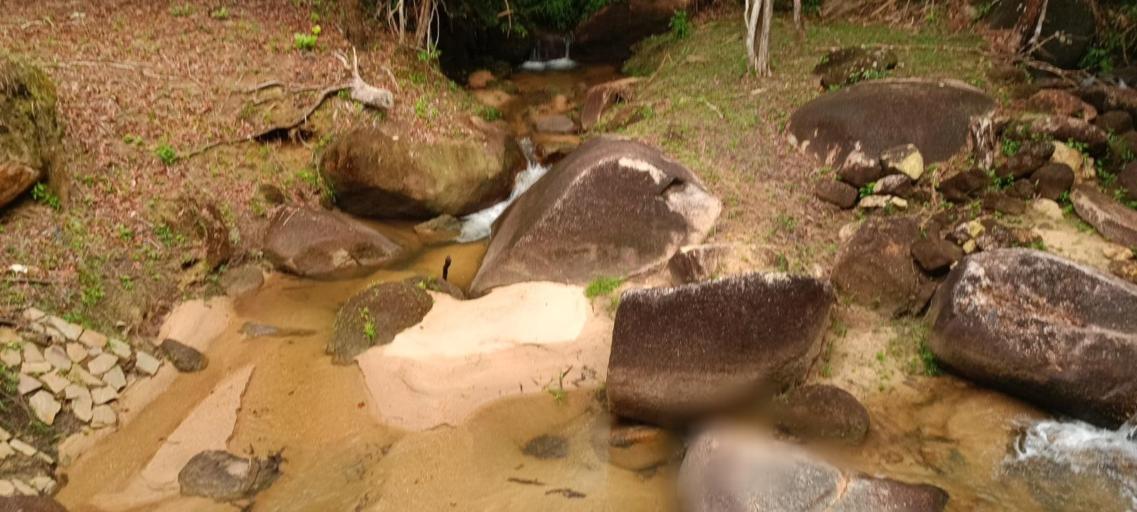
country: MY
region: Penang
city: Kampung Sungai Ara
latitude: 5.3935
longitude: 100.2582
